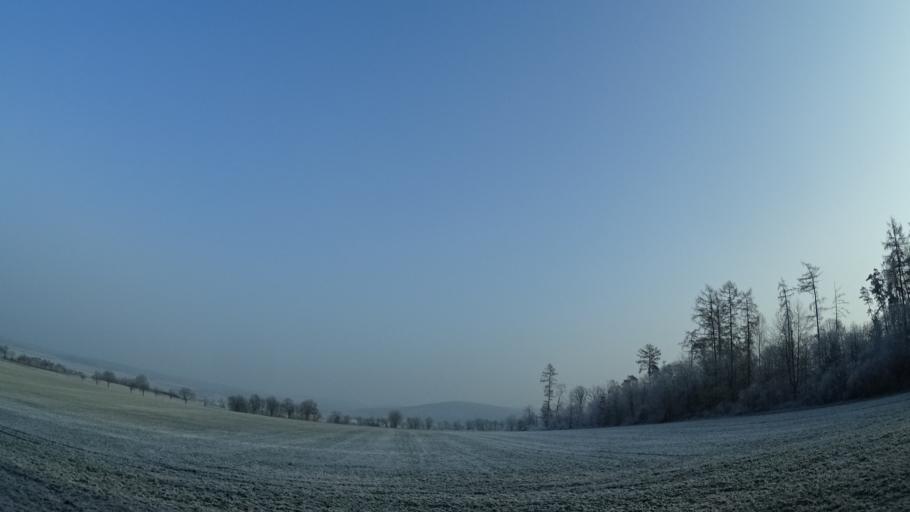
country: DE
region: Bavaria
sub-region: Upper Franconia
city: Sesslach
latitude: 50.2063
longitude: 10.8117
